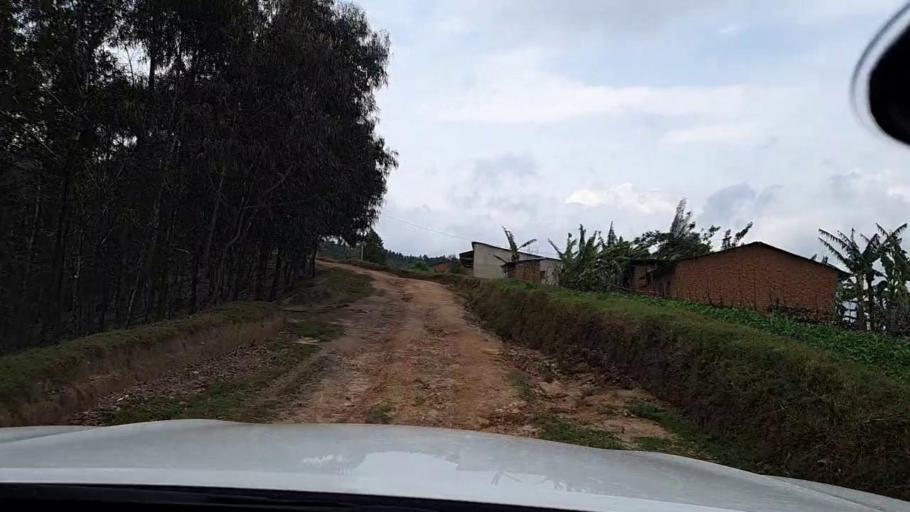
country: RW
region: Western Province
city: Kibuye
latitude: -2.1986
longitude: 29.3202
